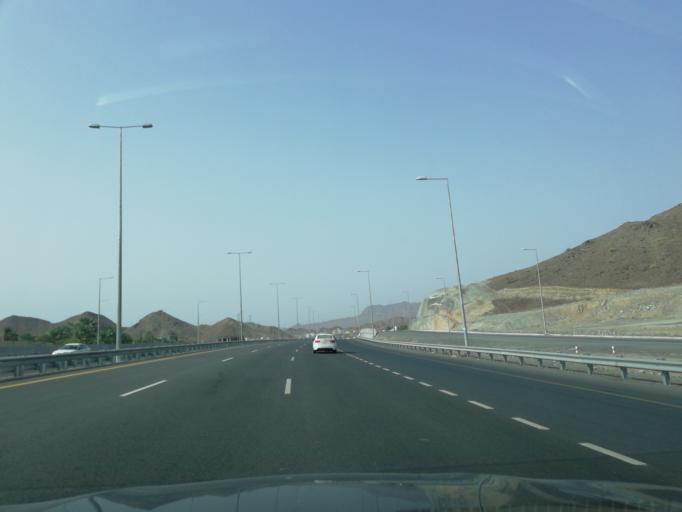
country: OM
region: Muhafazat ad Dakhiliyah
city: Bidbid
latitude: 23.4058
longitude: 58.0988
